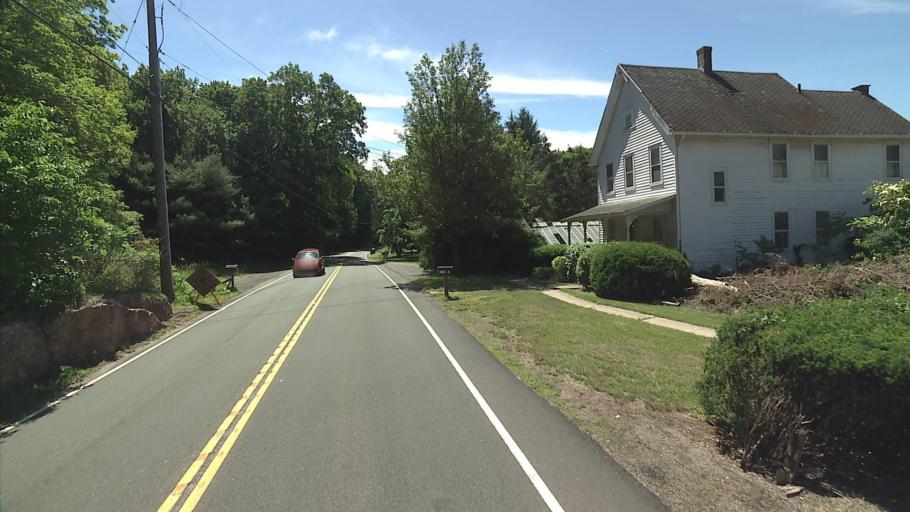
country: US
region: Connecticut
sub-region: New Haven County
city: Guilford
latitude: 41.3279
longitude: -72.7049
